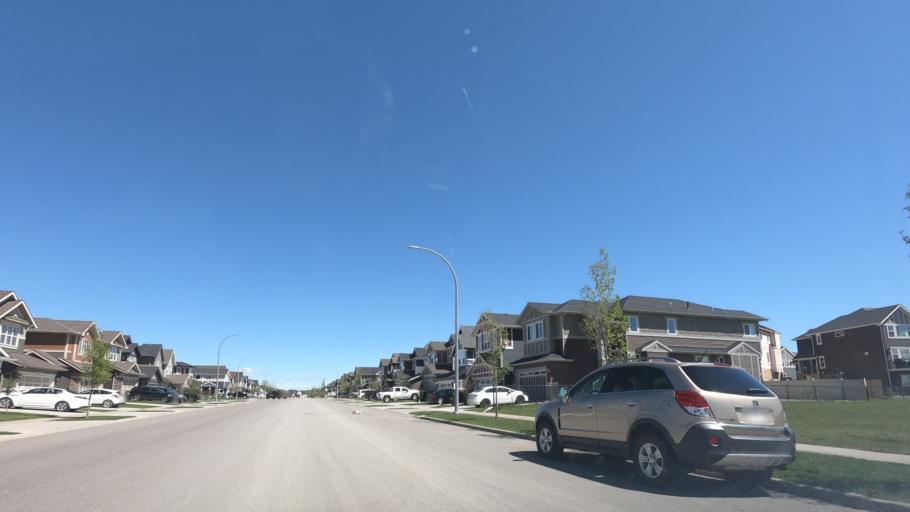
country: CA
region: Alberta
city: Airdrie
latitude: 51.2606
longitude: -113.9848
